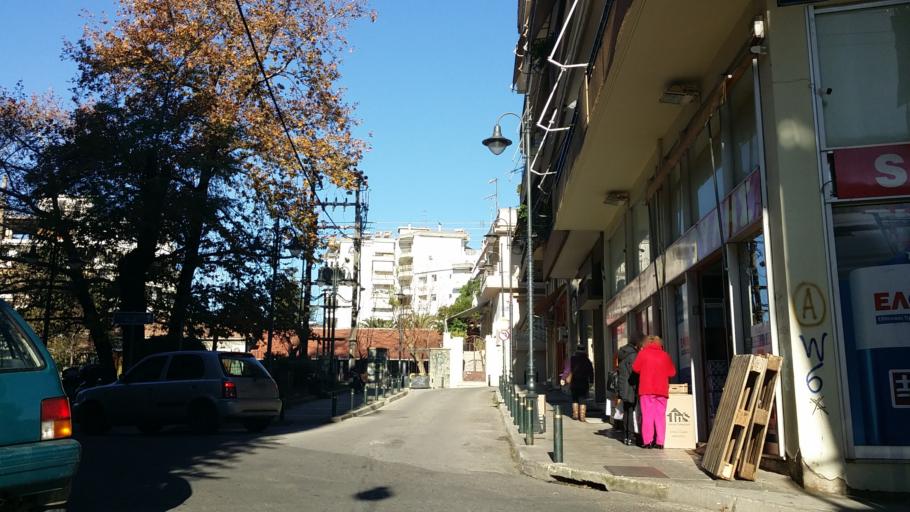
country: GR
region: West Greece
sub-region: Nomos Aitolias kai Akarnanias
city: Agrinio
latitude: 38.6268
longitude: 21.4121
